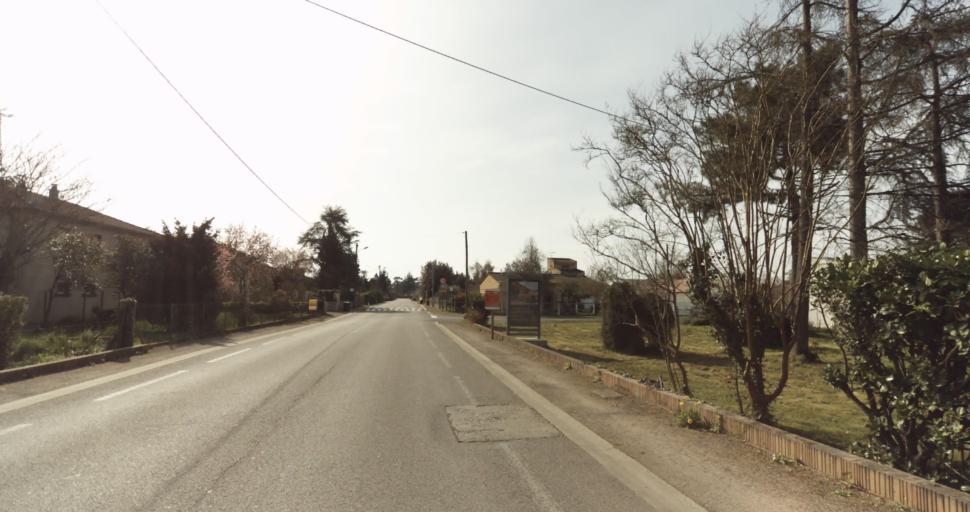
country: FR
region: Midi-Pyrenees
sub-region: Departement du Tarn
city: Saint-Sulpice-la-Pointe
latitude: 43.7828
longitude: 1.6794
